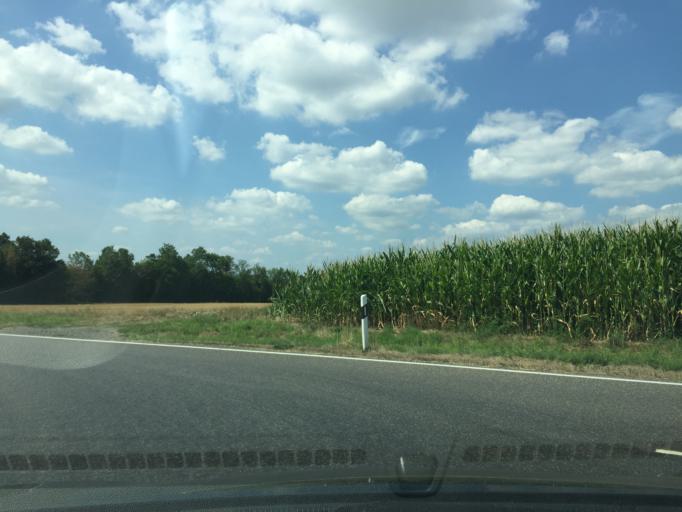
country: DE
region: Hesse
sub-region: Regierungsbezirk Giessen
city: Elz
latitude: 50.4641
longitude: 8.0607
